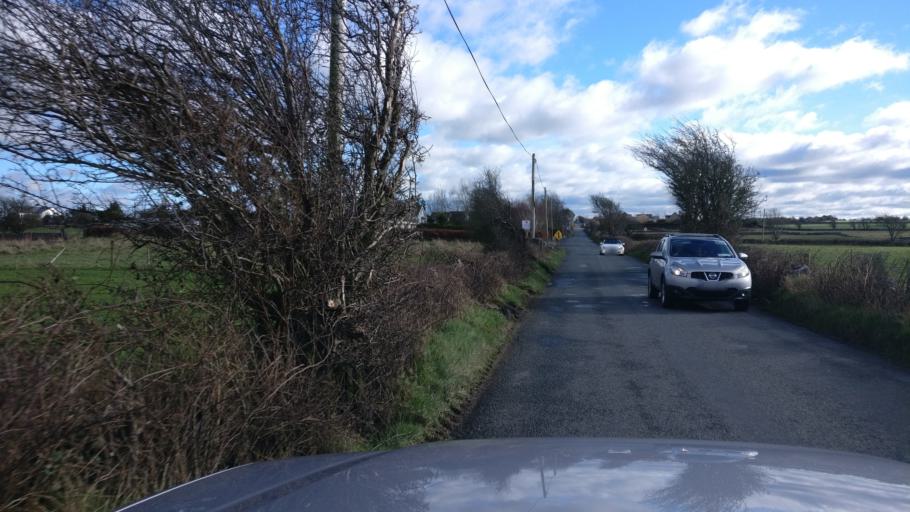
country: IE
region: Connaught
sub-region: County Galway
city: Oranmore
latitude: 53.2674
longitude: -8.8728
